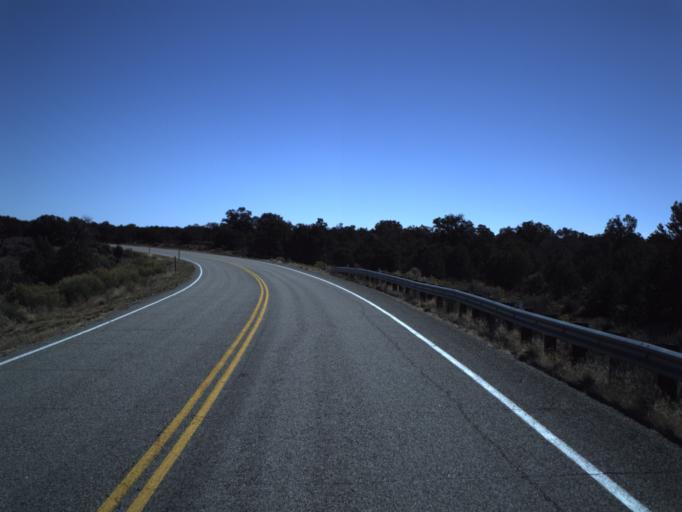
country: US
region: Utah
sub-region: San Juan County
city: Blanding
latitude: 37.5630
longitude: -110.0257
